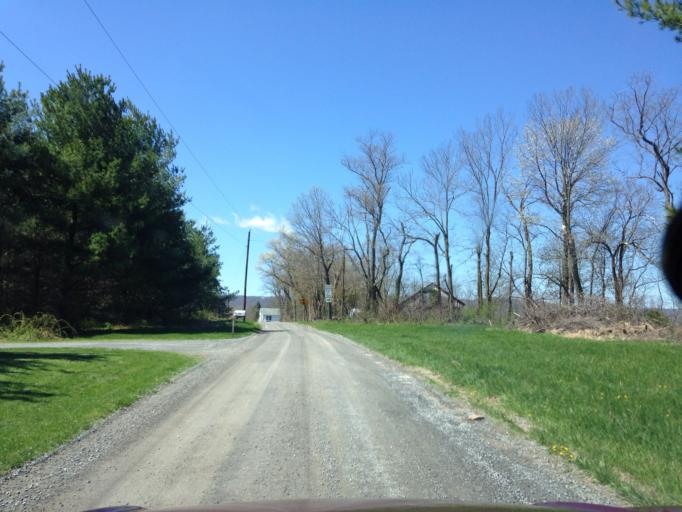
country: US
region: Maryland
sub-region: Frederick County
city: Brunswick
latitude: 39.2982
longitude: -77.6426
